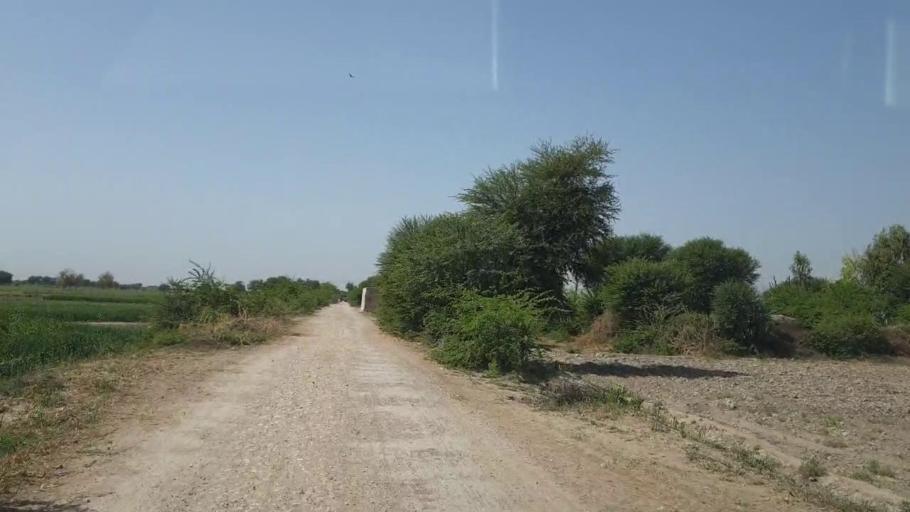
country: PK
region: Sindh
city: Naukot
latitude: 24.9077
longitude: 69.4871
